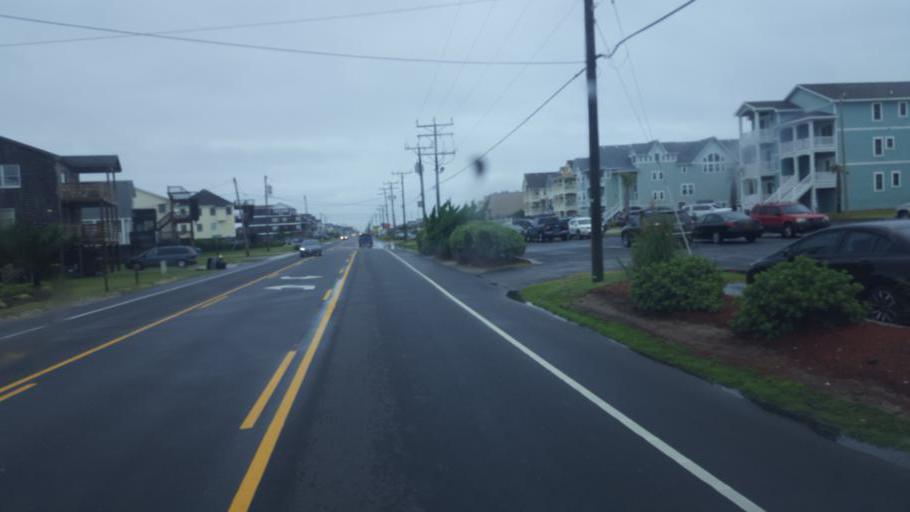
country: US
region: North Carolina
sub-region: Dare County
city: Nags Head
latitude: 35.9964
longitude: -75.6467
